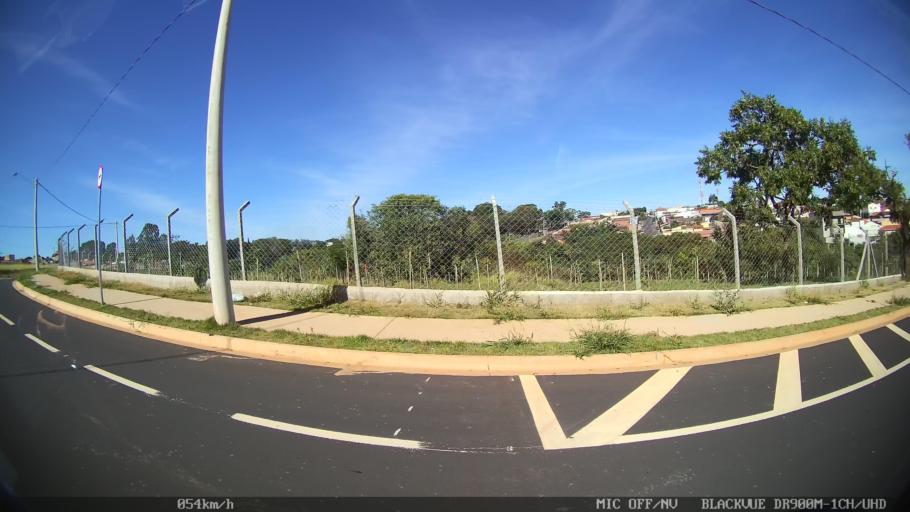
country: BR
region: Sao Paulo
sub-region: Franca
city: Franca
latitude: -20.5557
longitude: -47.3677
